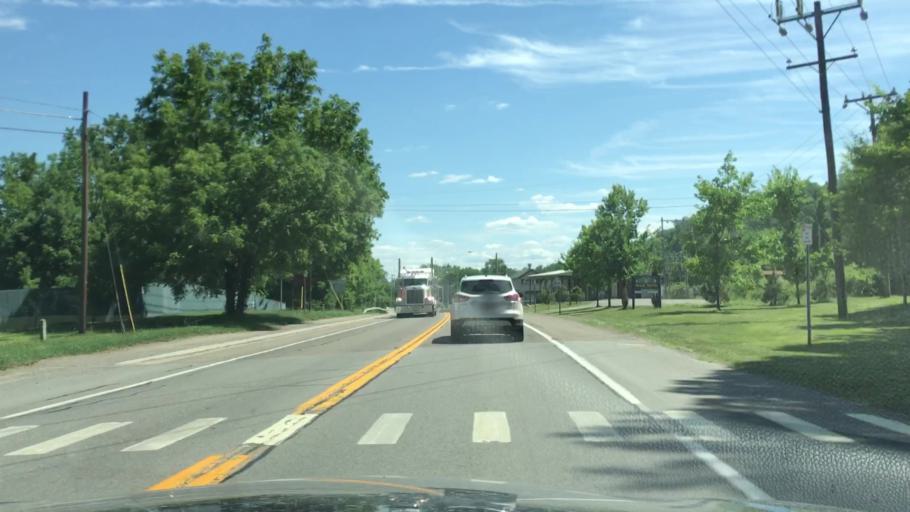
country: US
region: New York
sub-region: Livingston County
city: Mount Morris
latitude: 42.7402
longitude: -77.8824
